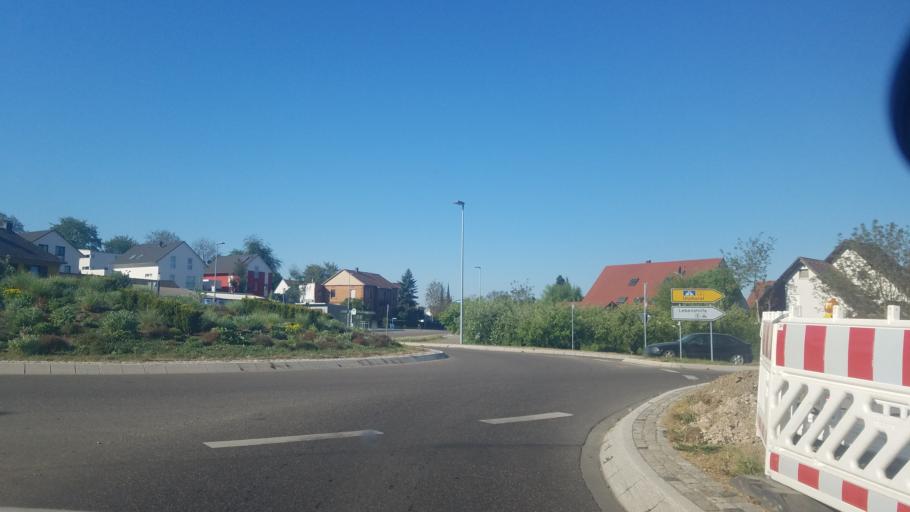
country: DE
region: Baden-Wuerttemberg
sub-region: Karlsruhe Region
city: Ottersweier
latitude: 48.6730
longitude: 8.1189
